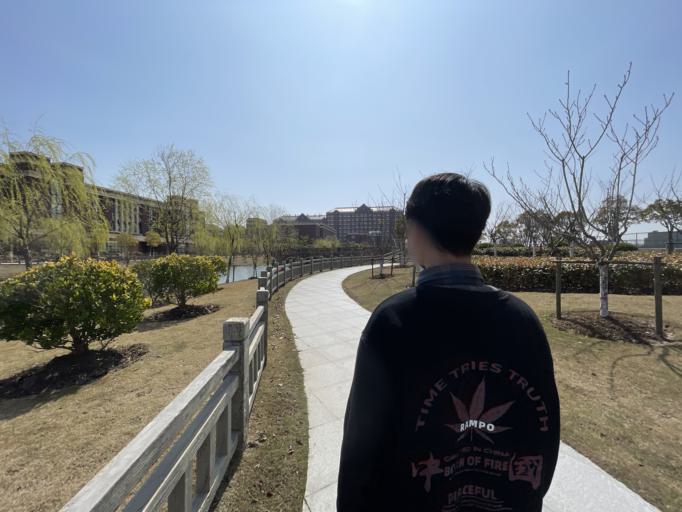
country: CN
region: Shanghai Shi
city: Shuyuan
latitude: 30.8935
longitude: 121.8855
